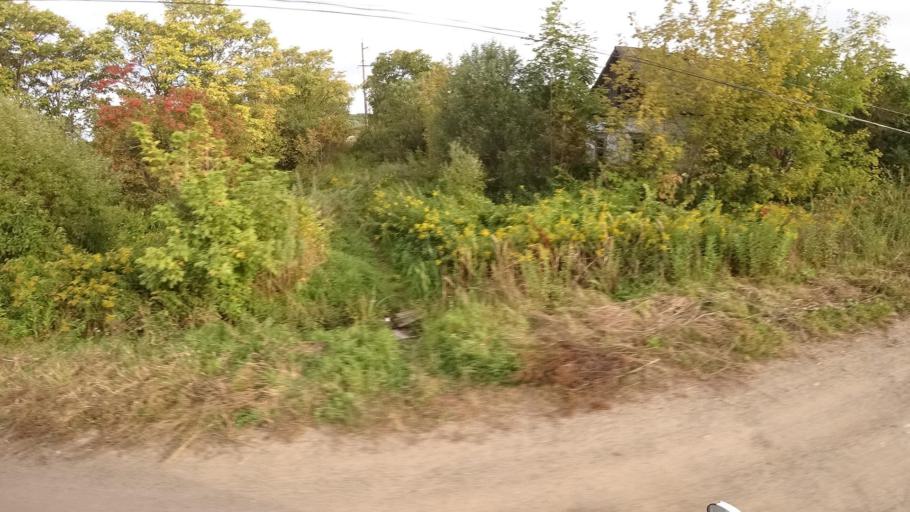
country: RU
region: Primorskiy
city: Yakovlevka
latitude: 44.4202
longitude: 133.4503
